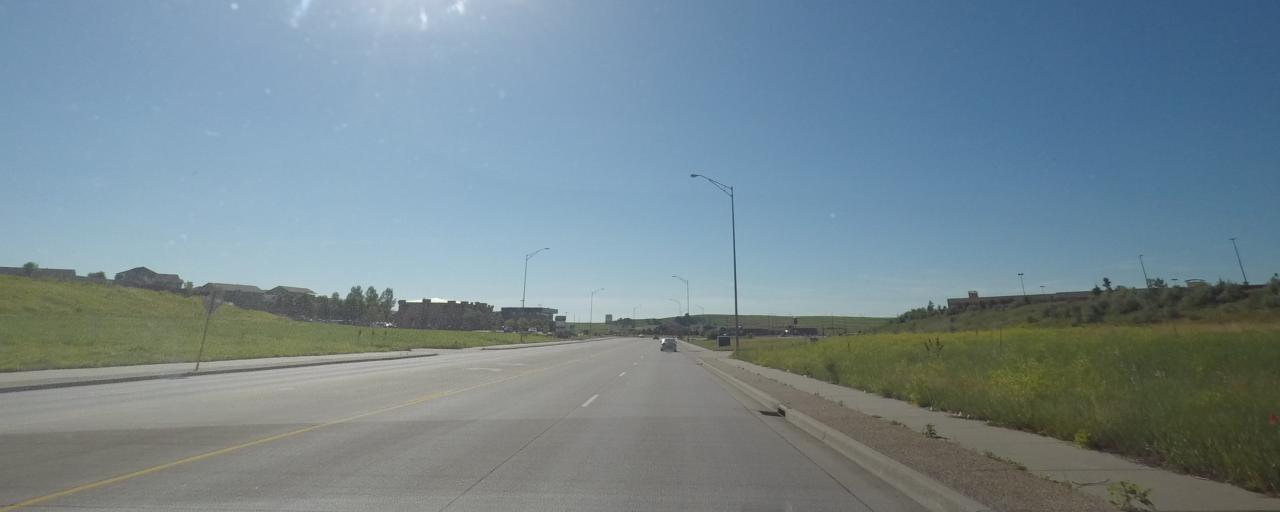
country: US
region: South Dakota
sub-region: Pennington County
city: Rapid City
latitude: 44.0358
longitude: -103.2168
